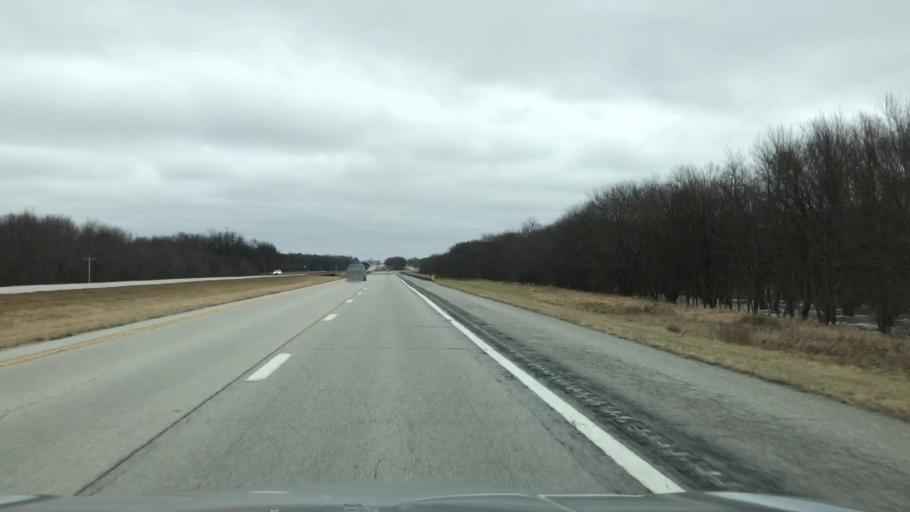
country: US
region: Missouri
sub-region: Linn County
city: Linneus
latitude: 39.7776
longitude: -93.3281
